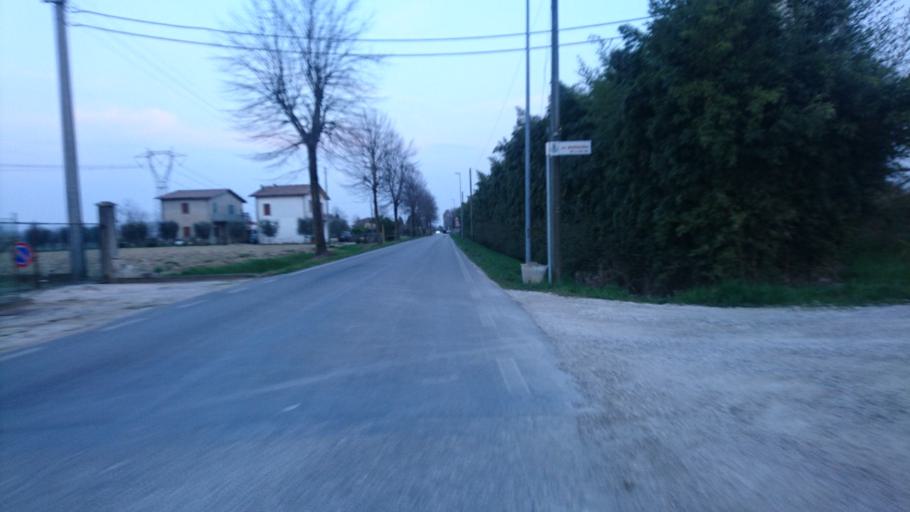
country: IT
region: Veneto
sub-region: Provincia di Padova
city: Saccolongo
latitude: 45.3923
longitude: 11.7485
